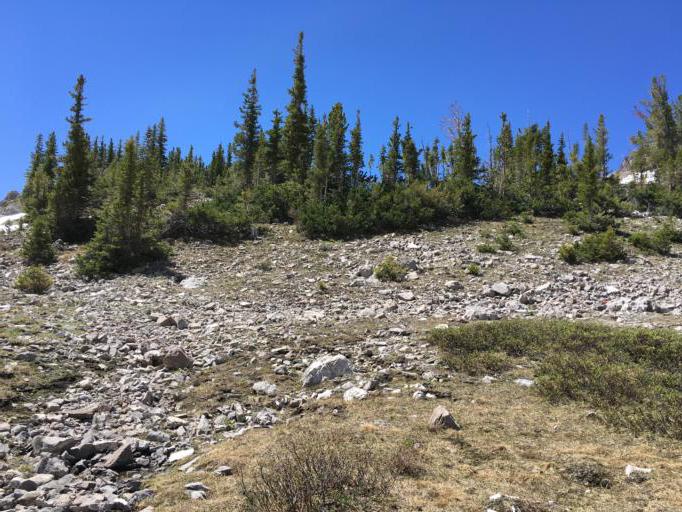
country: US
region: Wyoming
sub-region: Teton County
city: Moose Wilson Road
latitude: 43.5910
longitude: -110.8840
